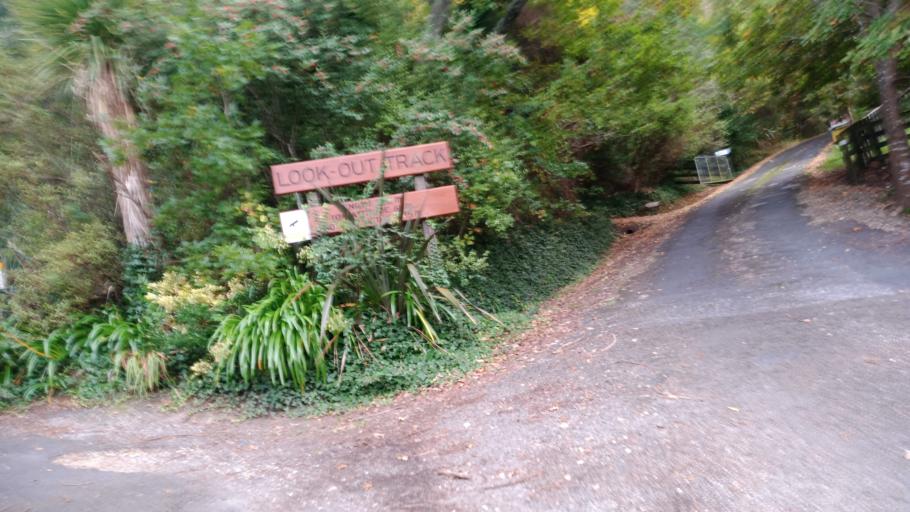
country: NZ
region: Gisborne
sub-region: Gisborne District
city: Gisborne
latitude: -38.6517
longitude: 178.0256
